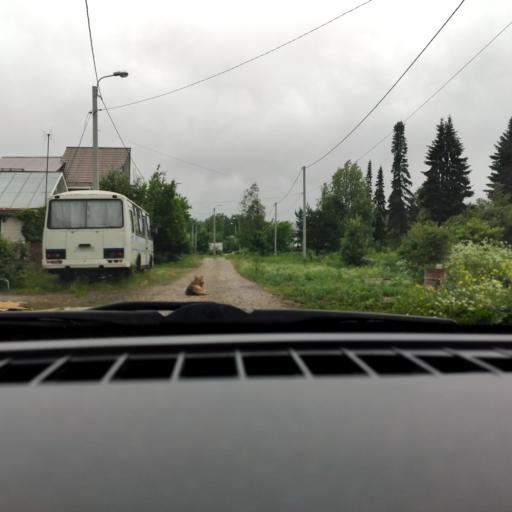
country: RU
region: Perm
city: Froly
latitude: 57.9742
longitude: 56.3085
